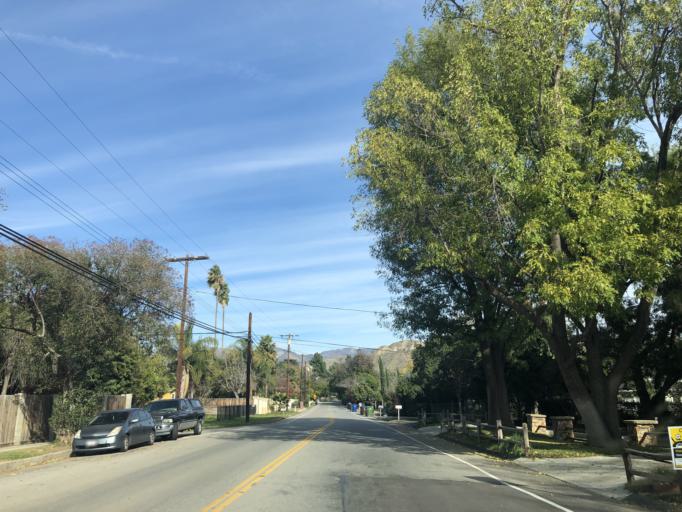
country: US
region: California
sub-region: Los Angeles County
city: San Fernando
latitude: 34.2782
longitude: -118.3766
